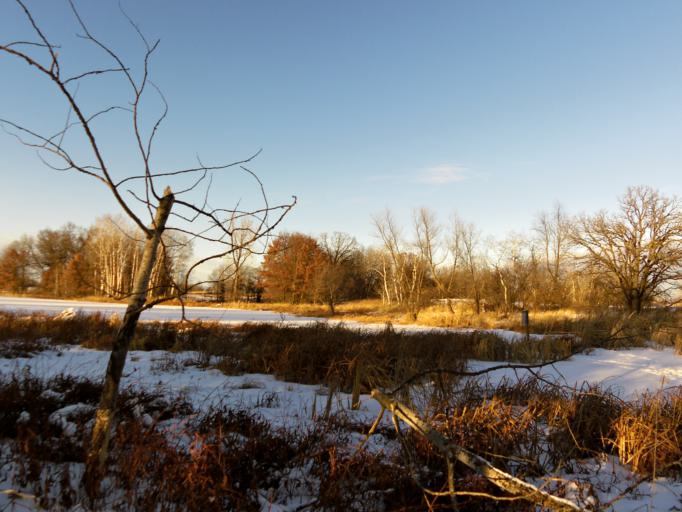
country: US
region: Minnesota
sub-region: Washington County
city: Lake Elmo
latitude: 44.9821
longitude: -92.9066
